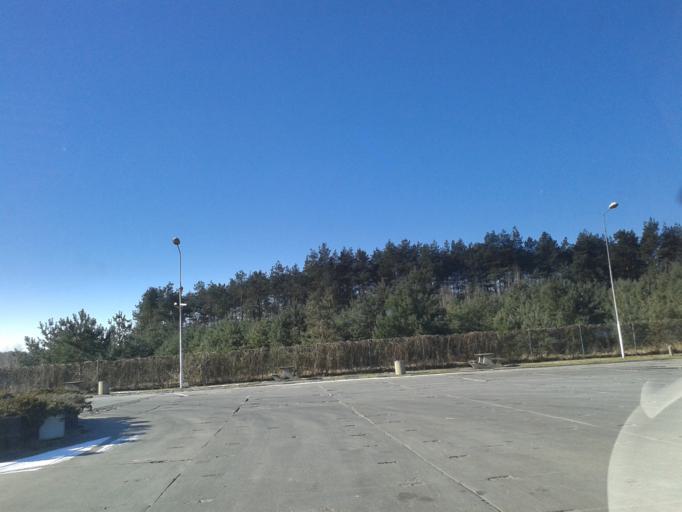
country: PL
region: Greater Poland Voivodeship
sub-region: Powiat pilski
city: Osiek nad Notecia
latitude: 53.1549
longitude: 17.3275
